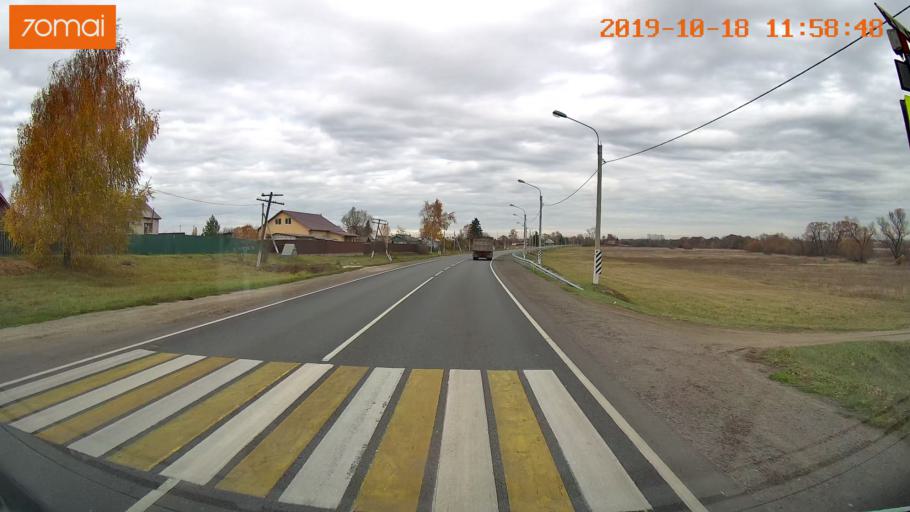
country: RU
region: Rjazan
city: Zakharovo
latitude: 54.2754
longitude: 39.1698
